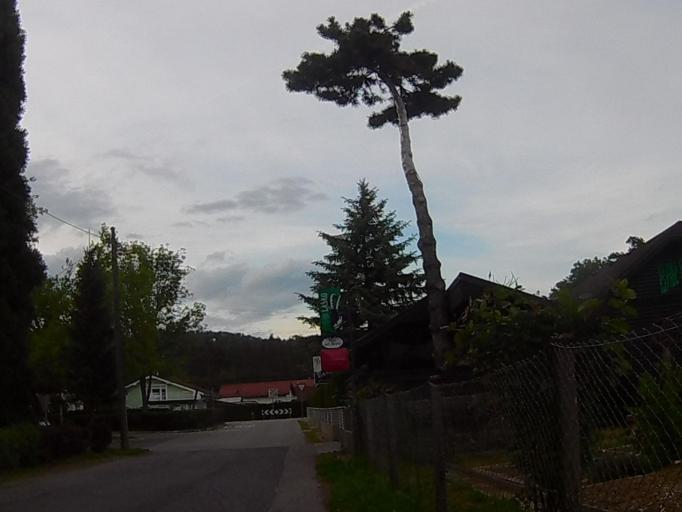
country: SI
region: Maribor
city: Pekre
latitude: 46.5616
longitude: 15.6021
